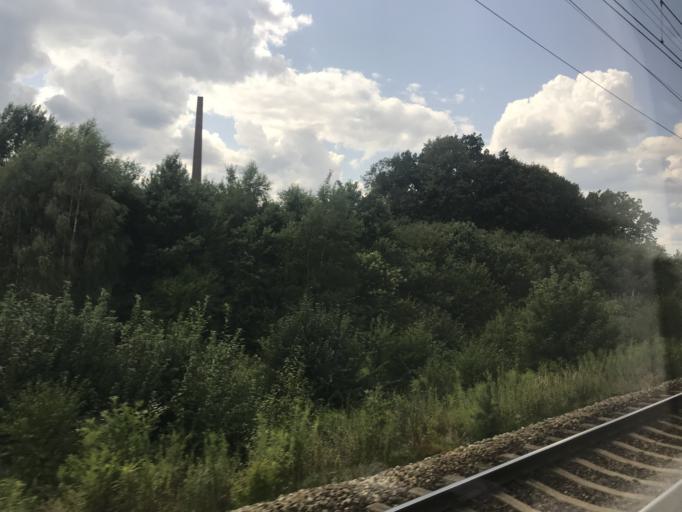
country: PL
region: Lubusz
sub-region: Powiat sulecinski
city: Torzym
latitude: 52.3234
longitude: 15.0023
